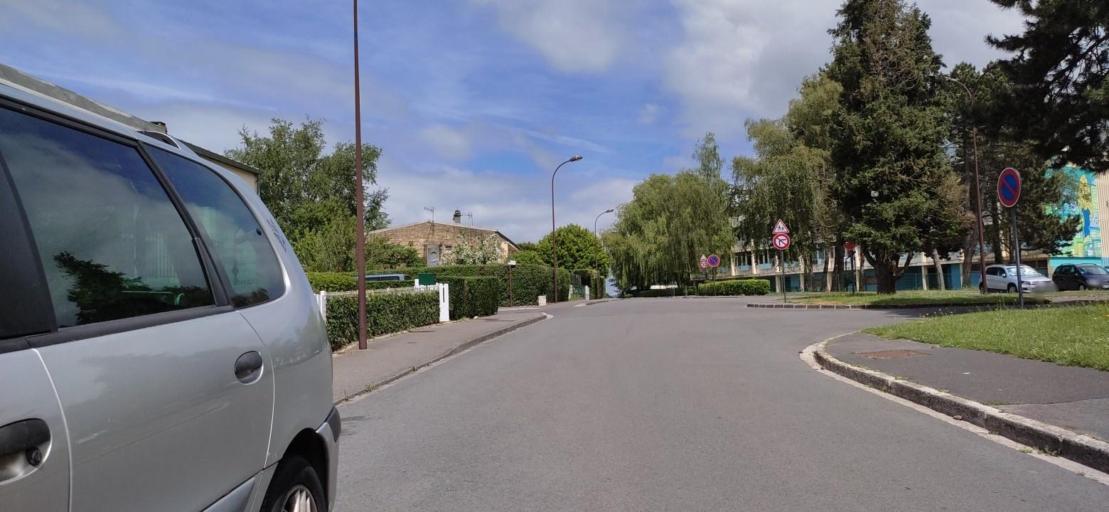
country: FR
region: Picardie
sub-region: Departement de l'Aisne
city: Saint-Quentin
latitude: 49.8608
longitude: 3.2972
